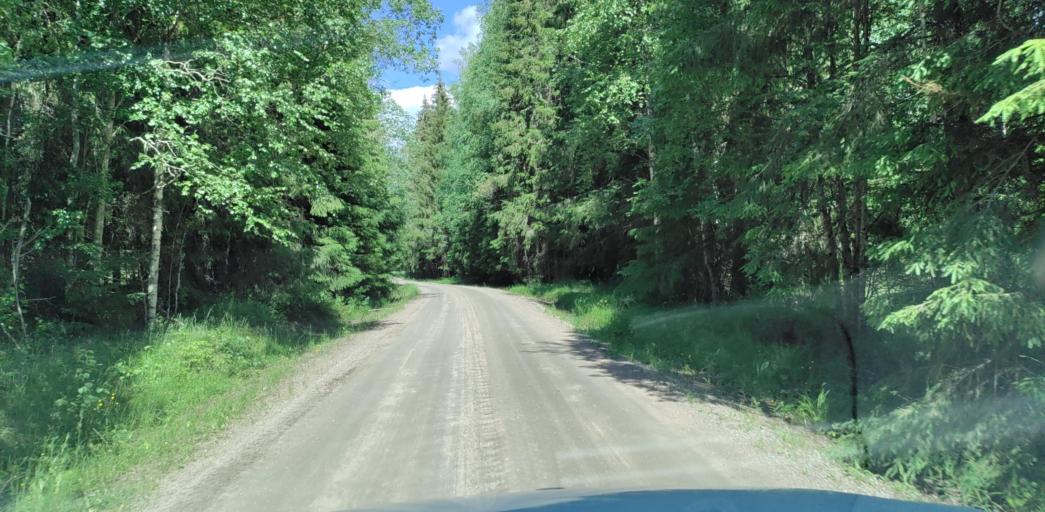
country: SE
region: Vaermland
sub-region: Sunne Kommun
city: Sunne
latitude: 60.0441
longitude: 13.2551
